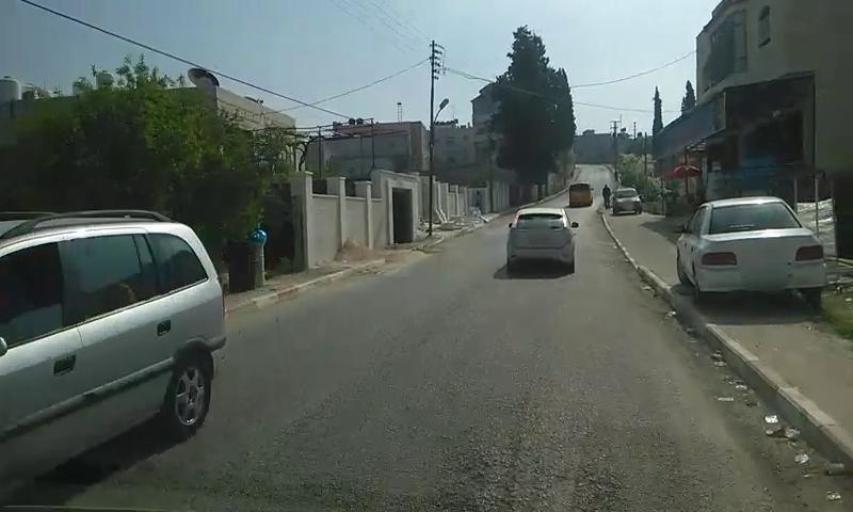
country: PS
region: West Bank
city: `Ayn Yabrud
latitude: 31.9546
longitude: 35.2478
